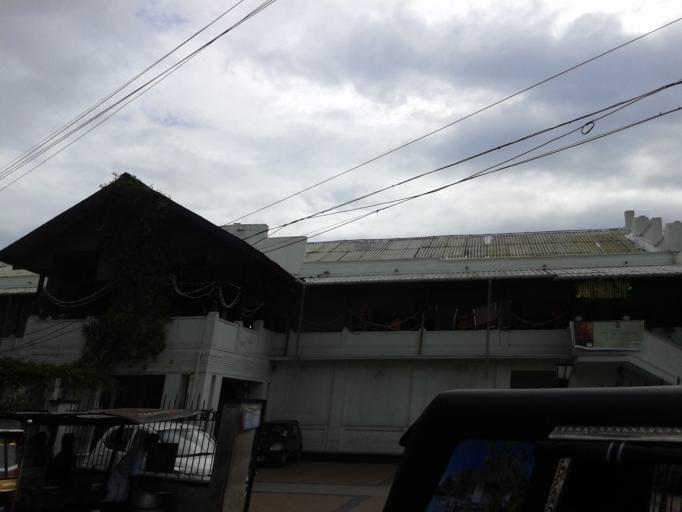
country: IN
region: Kerala
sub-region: Kozhikode
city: Kozhikode
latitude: 11.2535
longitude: 75.7793
